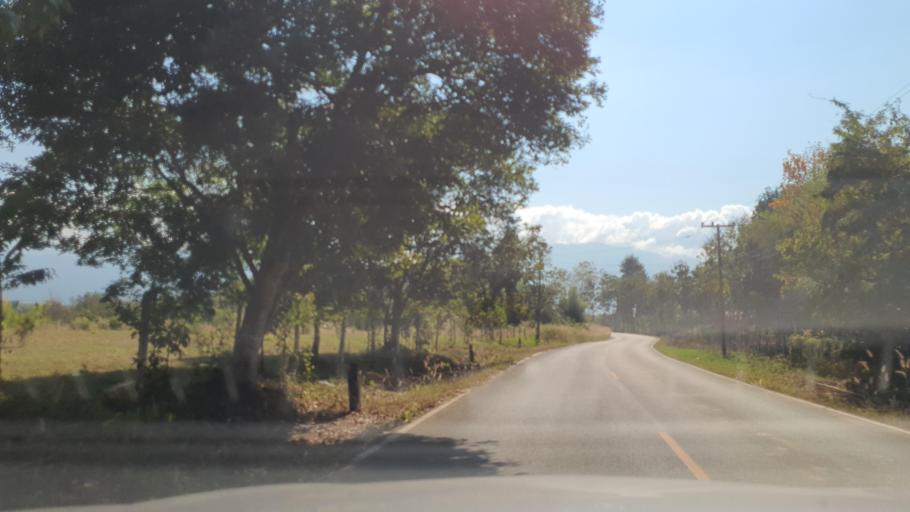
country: TH
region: Nan
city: Pua
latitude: 19.1517
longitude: 100.9128
